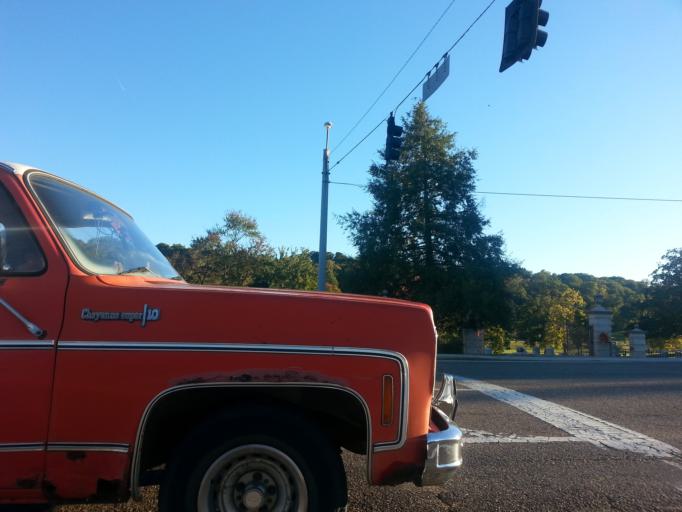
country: US
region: Tennessee
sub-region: Knox County
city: Knoxville
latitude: 35.9754
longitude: -83.9655
